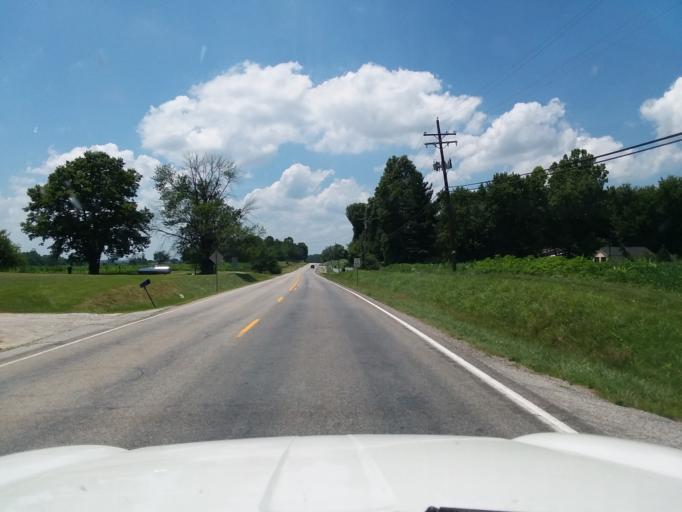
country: US
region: Indiana
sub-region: Johnson County
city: Trafalgar
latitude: 39.3715
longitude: -86.2686
